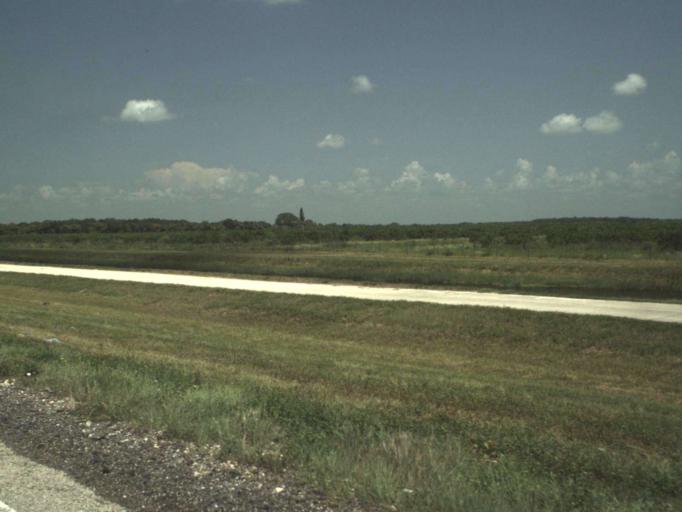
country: US
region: Florida
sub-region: Saint Lucie County
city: Fort Pierce South
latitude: 27.3681
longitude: -80.5473
